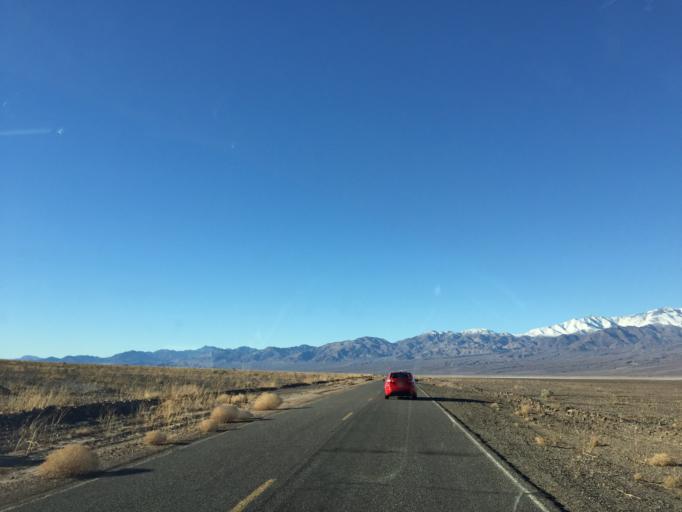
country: US
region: California
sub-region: San Bernardino County
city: Searles Valley
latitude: 36.1376
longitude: -116.7667
